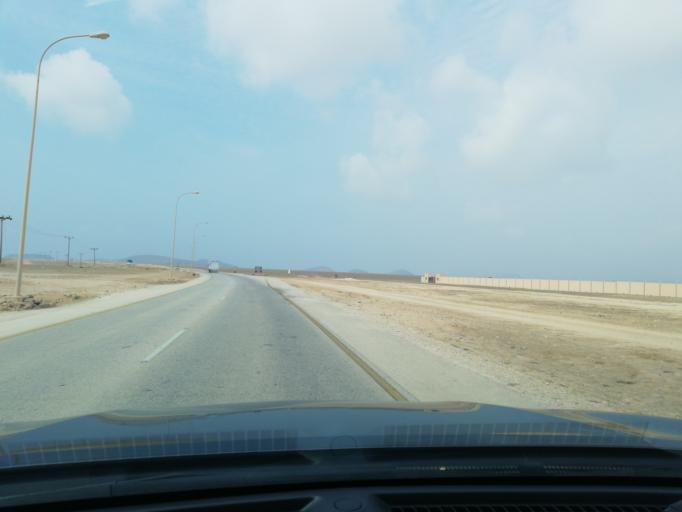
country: OM
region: Zufar
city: Salalah
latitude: 16.9399
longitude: 53.8449
